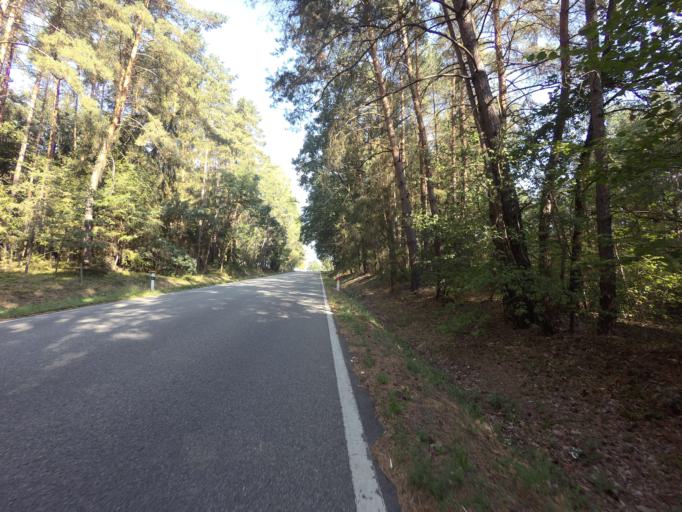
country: CZ
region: Jihocesky
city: Tyn nad Vltavou
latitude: 49.2687
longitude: 14.4091
